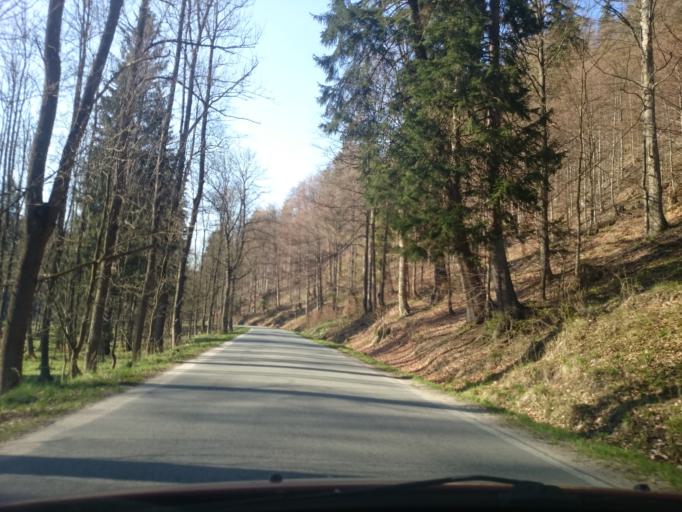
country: PL
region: Lower Silesian Voivodeship
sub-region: Powiat klodzki
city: Duszniki-Zdroj
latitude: 50.3556
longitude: 16.3967
